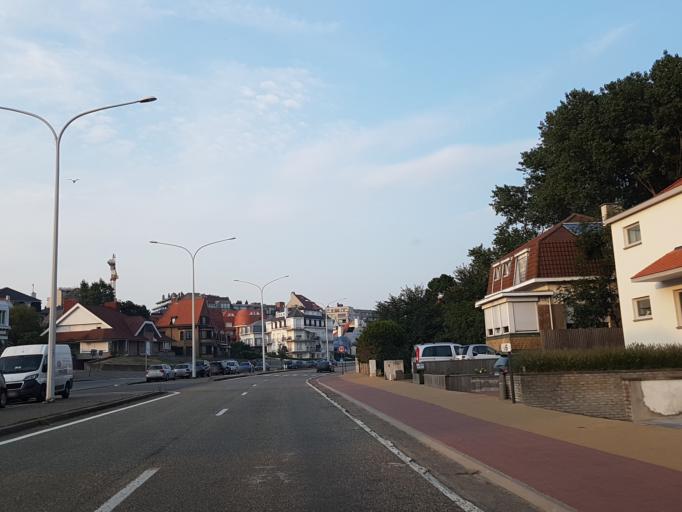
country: BE
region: Flanders
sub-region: Provincie West-Vlaanderen
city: Knokke-Heist
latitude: 51.3432
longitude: 3.2671
